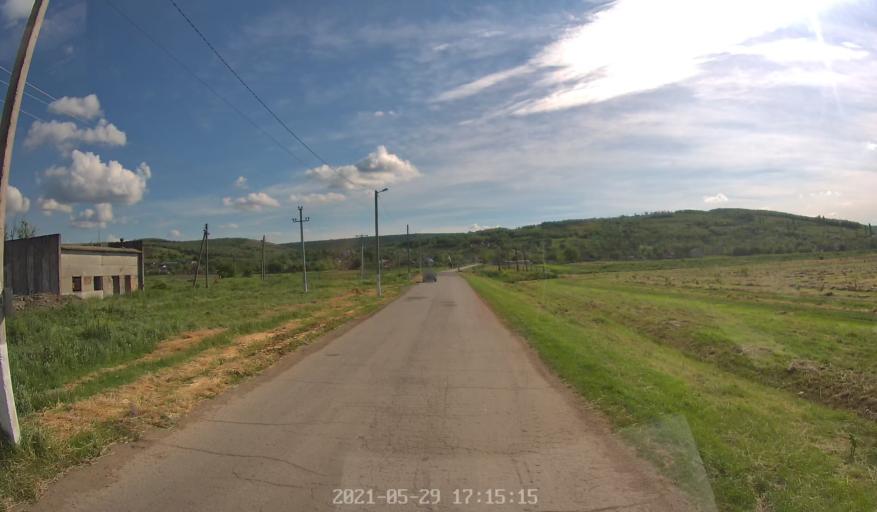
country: MD
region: Laloveni
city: Ialoveni
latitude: 46.8326
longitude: 28.8466
